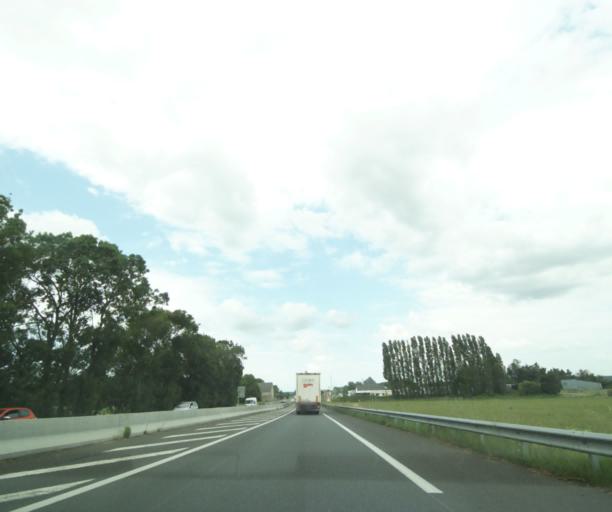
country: FR
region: Pays de la Loire
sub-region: Departement de Maine-et-Loire
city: Vivy
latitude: 47.3024
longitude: -0.0371
